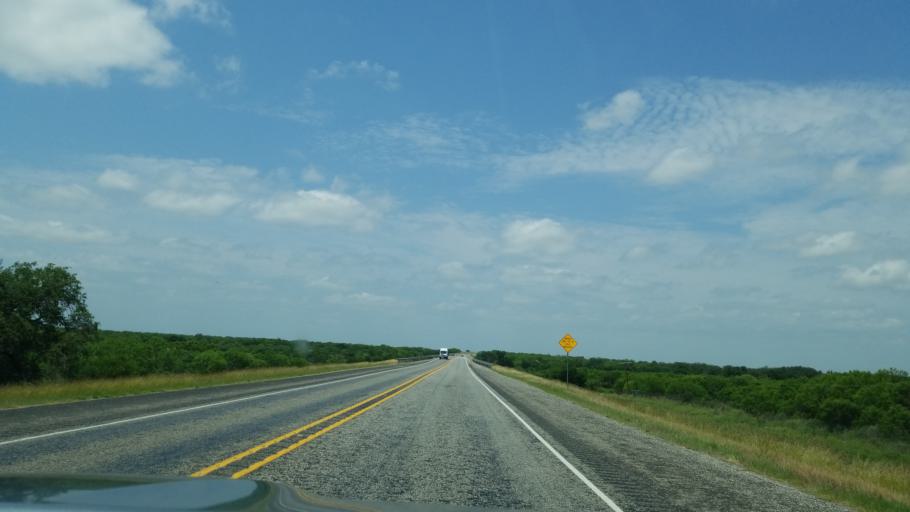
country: US
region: Texas
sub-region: Zavala County
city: La Pryor
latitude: 28.9348
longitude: -99.7910
